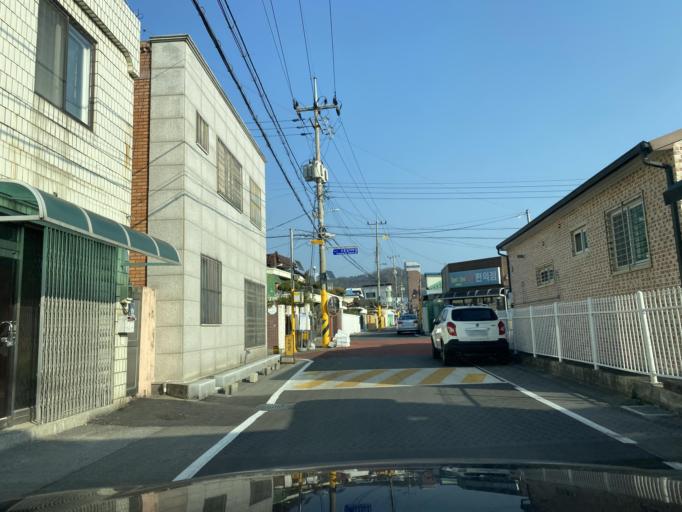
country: KR
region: Chungcheongnam-do
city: Yesan
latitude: 36.6775
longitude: 126.8454
